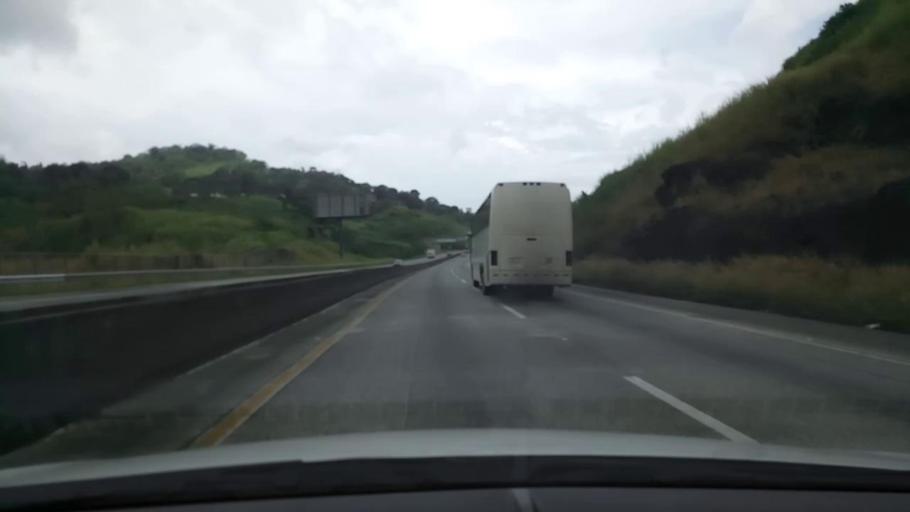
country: PA
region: Colon
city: Gatun
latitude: 9.2831
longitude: -79.7483
